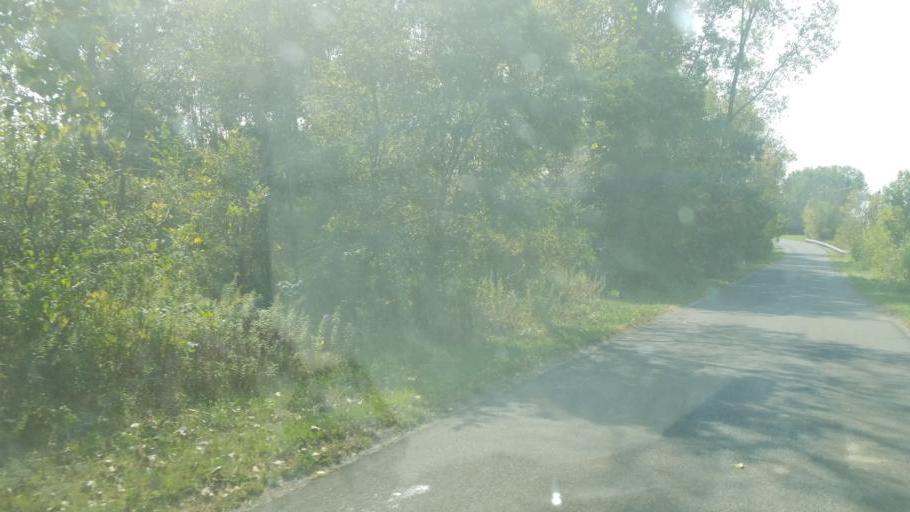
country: US
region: Ohio
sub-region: Crawford County
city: Galion
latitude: 40.7097
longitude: -82.7927
